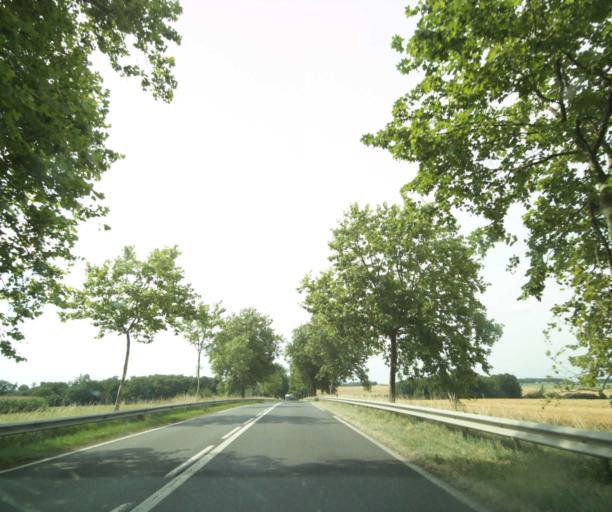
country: FR
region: Centre
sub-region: Departement d'Indre-et-Loire
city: Saint-Paterne-Racan
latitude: 47.5997
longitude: 0.5227
